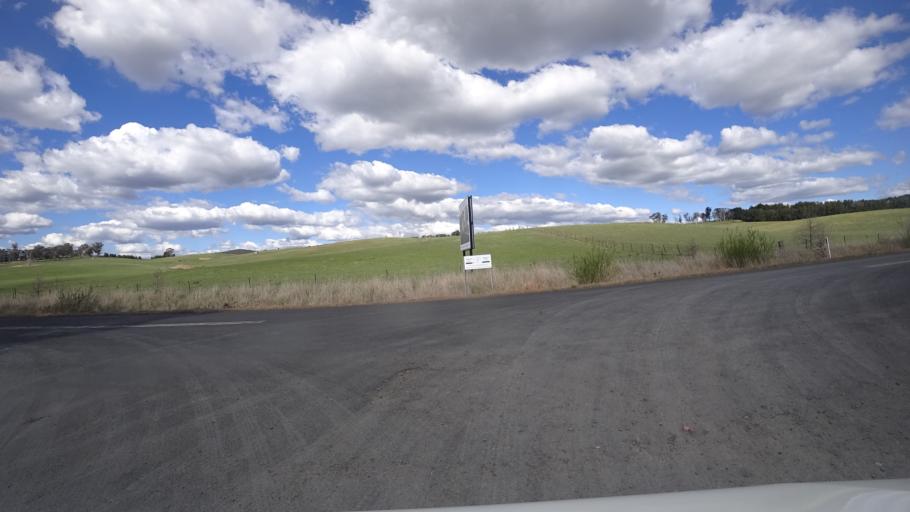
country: AU
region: New South Wales
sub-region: Oberon
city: Oberon
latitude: -33.6656
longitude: 149.7790
